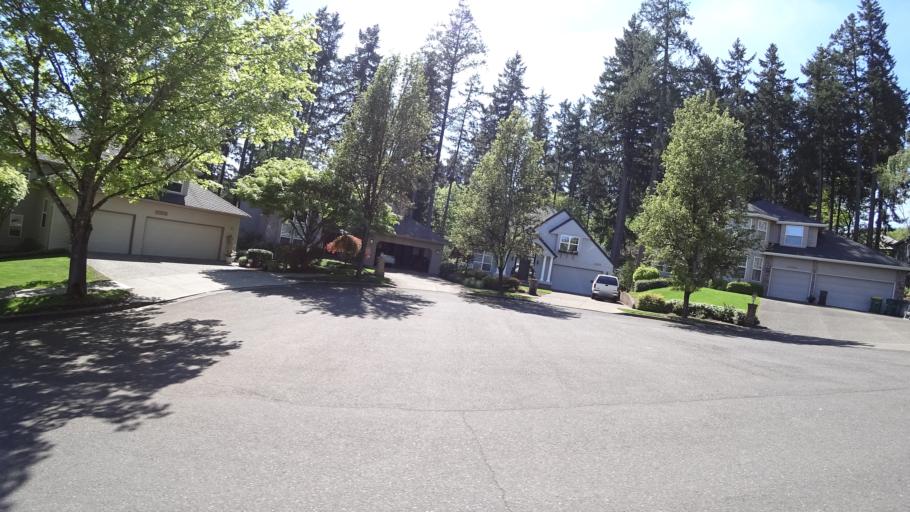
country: US
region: Oregon
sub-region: Washington County
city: Aloha
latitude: 45.4450
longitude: -122.8450
